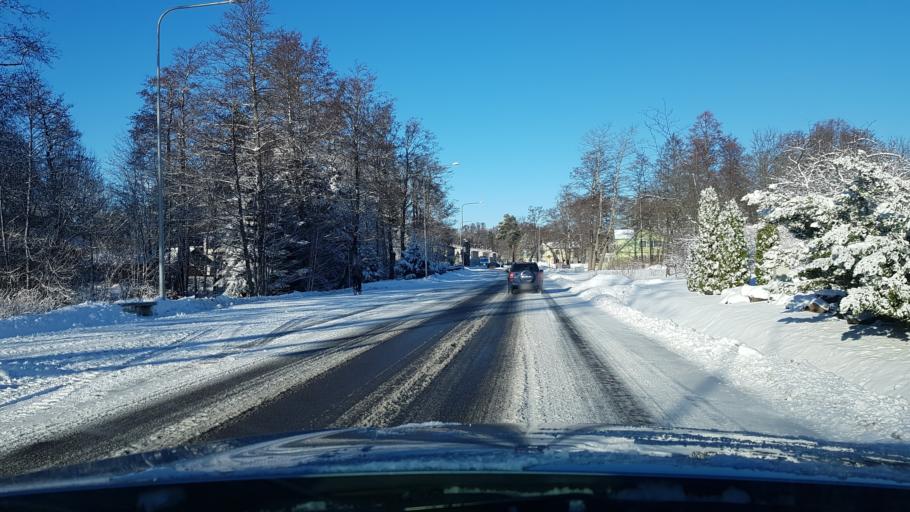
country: EE
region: Hiiumaa
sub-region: Kaerdla linn
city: Kardla
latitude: 58.9923
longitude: 22.7476
